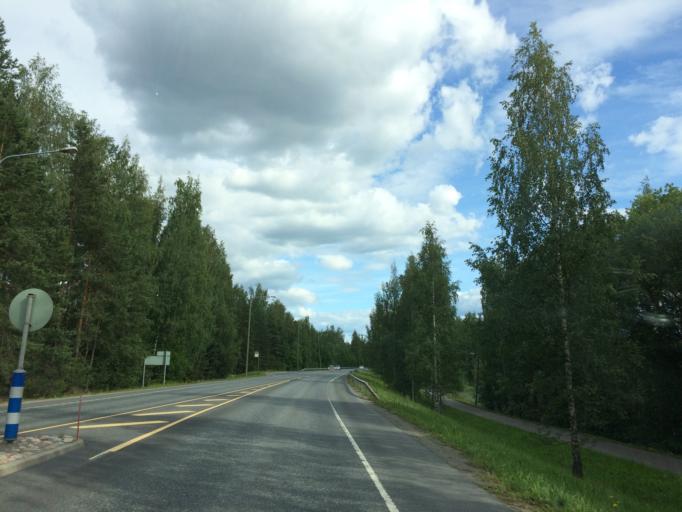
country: FI
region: Haeme
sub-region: Haemeenlinna
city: Haemeenlinna
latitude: 60.9793
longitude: 24.5288
